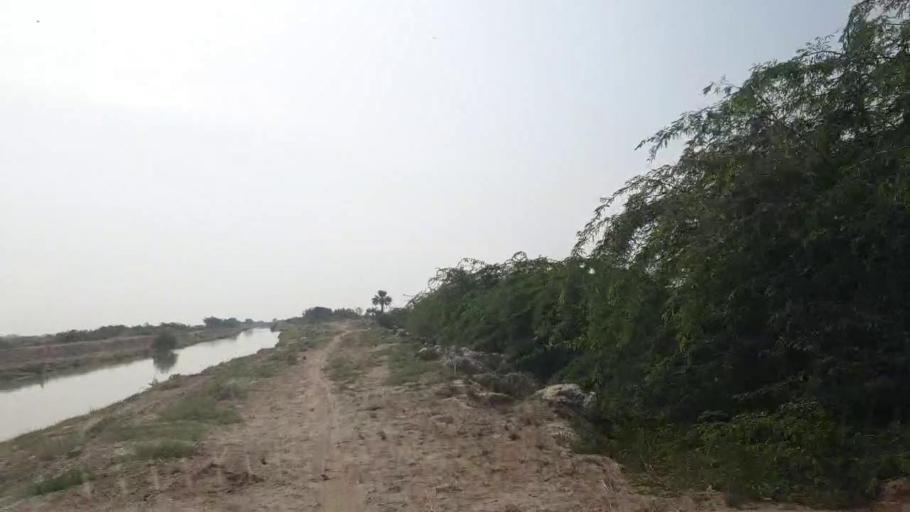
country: PK
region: Sindh
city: Badin
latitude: 24.5628
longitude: 68.8500
